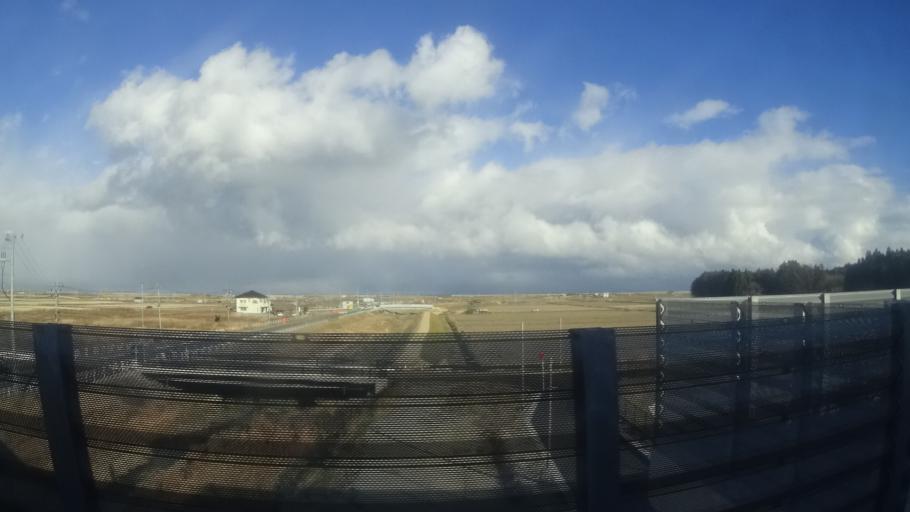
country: JP
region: Miyagi
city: Watari
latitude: 37.9244
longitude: 140.9009
